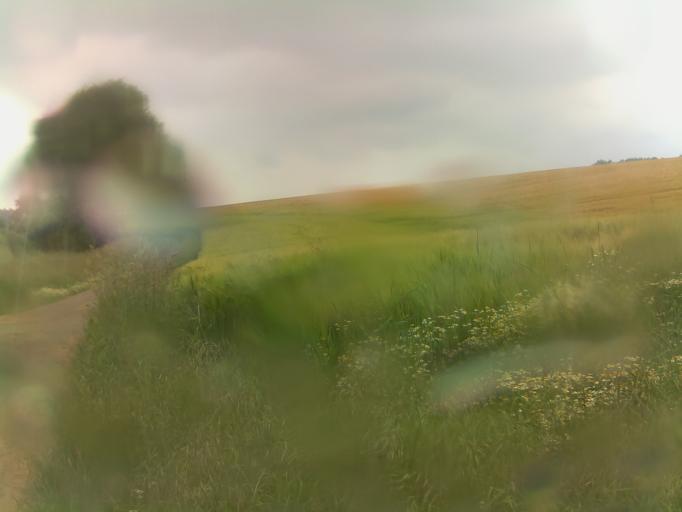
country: DE
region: Hesse
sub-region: Regierungsbezirk Giessen
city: Schlitz
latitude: 50.6710
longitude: 9.5367
